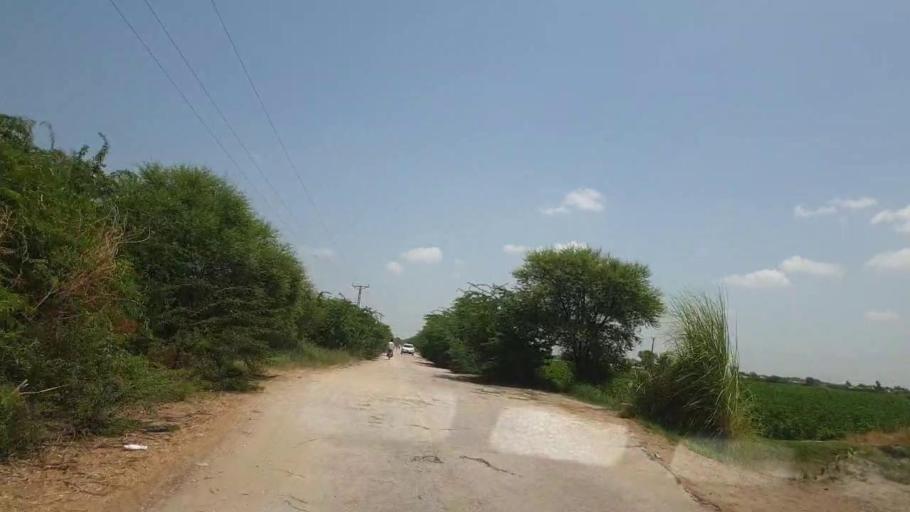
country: PK
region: Sindh
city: Pano Aqil
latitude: 27.6677
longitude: 69.2269
